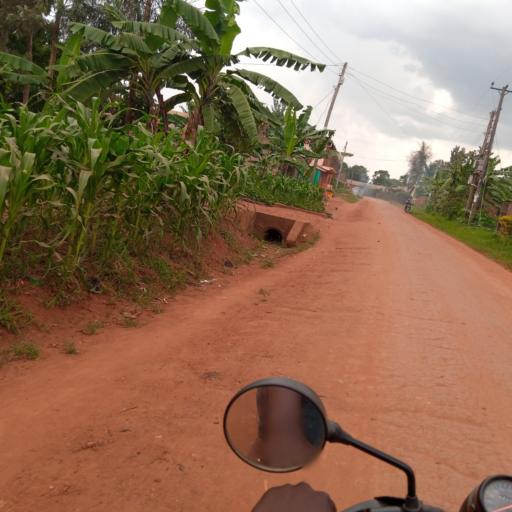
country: UG
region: Eastern Region
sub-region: Mbale District
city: Mbale
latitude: 1.1073
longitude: 34.1760
